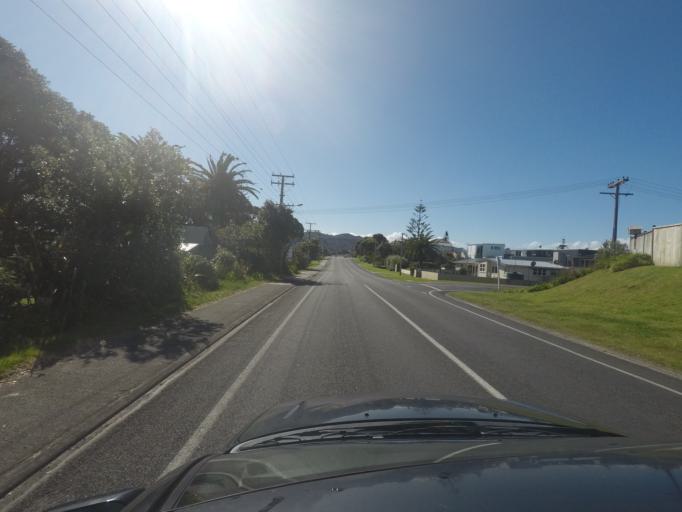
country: NZ
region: Bay of Plenty
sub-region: Western Bay of Plenty District
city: Waihi Beach
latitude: -37.4164
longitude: 175.9484
